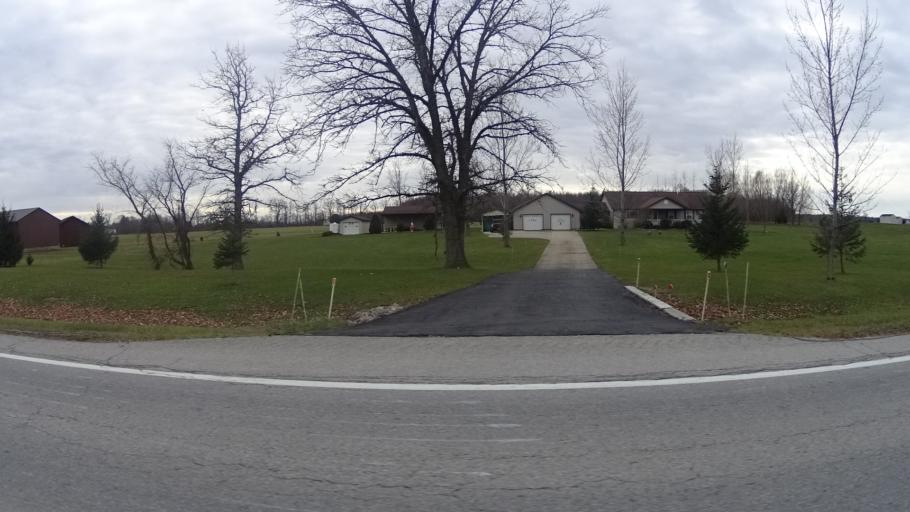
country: US
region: Ohio
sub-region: Lorain County
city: Camden
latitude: 41.1724
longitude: -82.3361
